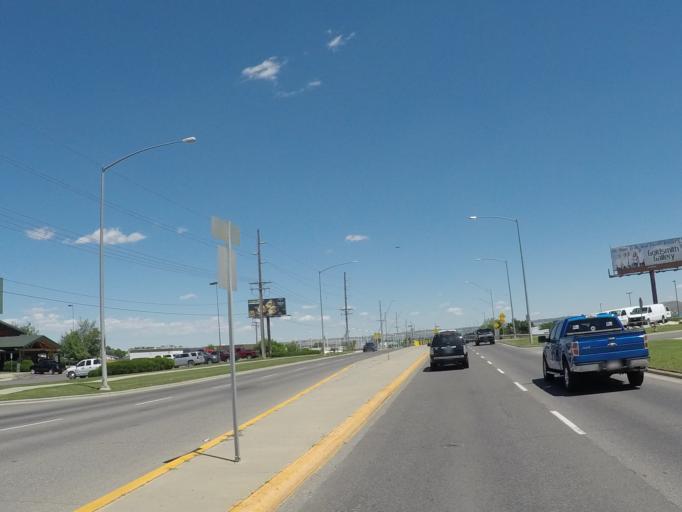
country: US
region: Montana
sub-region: Yellowstone County
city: Billings
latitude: 45.7552
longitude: -108.5903
